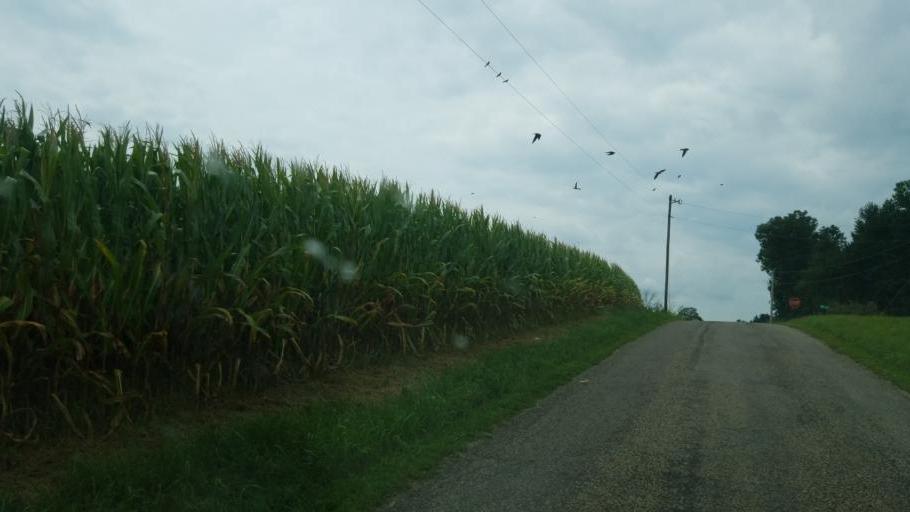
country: US
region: Ohio
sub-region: Ashland County
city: Loudonville
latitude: 40.5657
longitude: -82.2773
